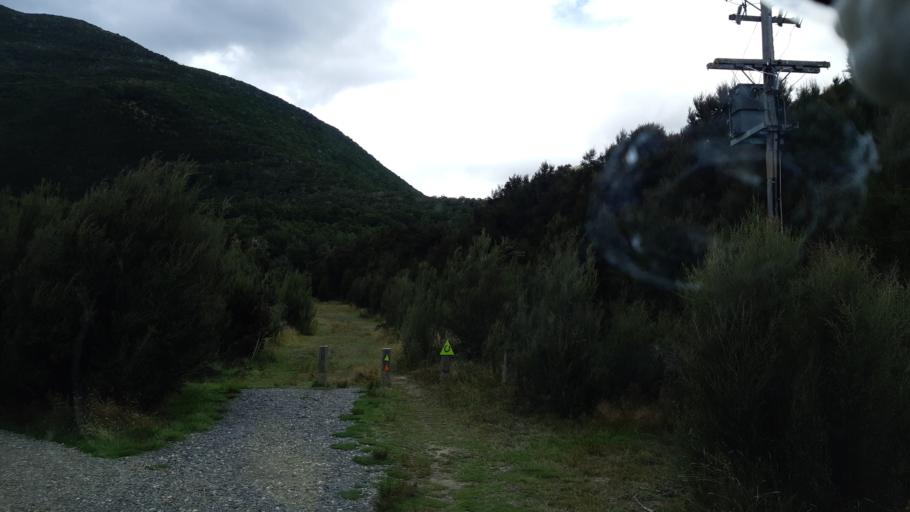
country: NZ
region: Canterbury
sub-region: Hurunui District
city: Amberley
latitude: -42.5167
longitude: 172.3865
